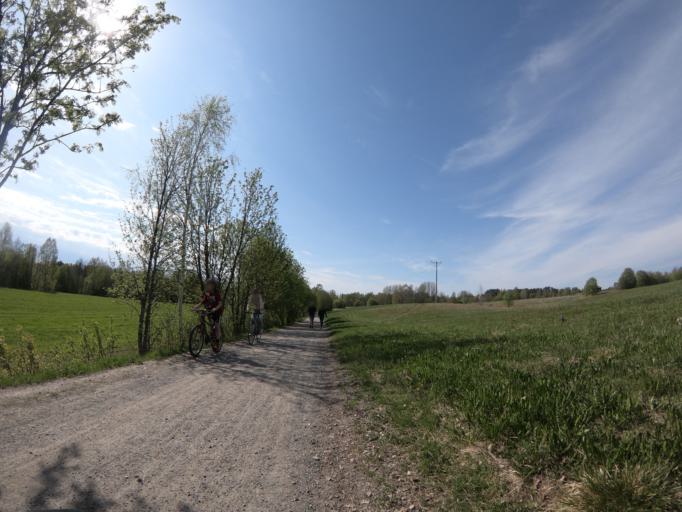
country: SE
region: Vaesterbotten
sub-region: Umea Kommun
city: Roback
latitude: 63.8293
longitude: 20.1865
